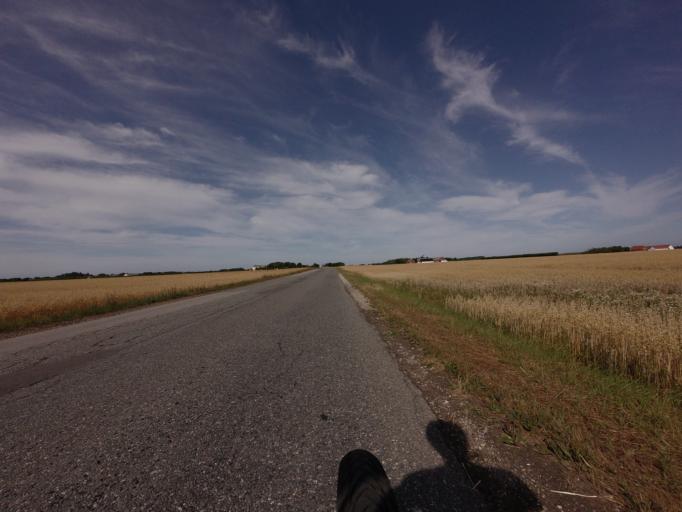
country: DK
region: North Denmark
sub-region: Hjorring Kommune
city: Vra
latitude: 57.4146
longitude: 9.8713
